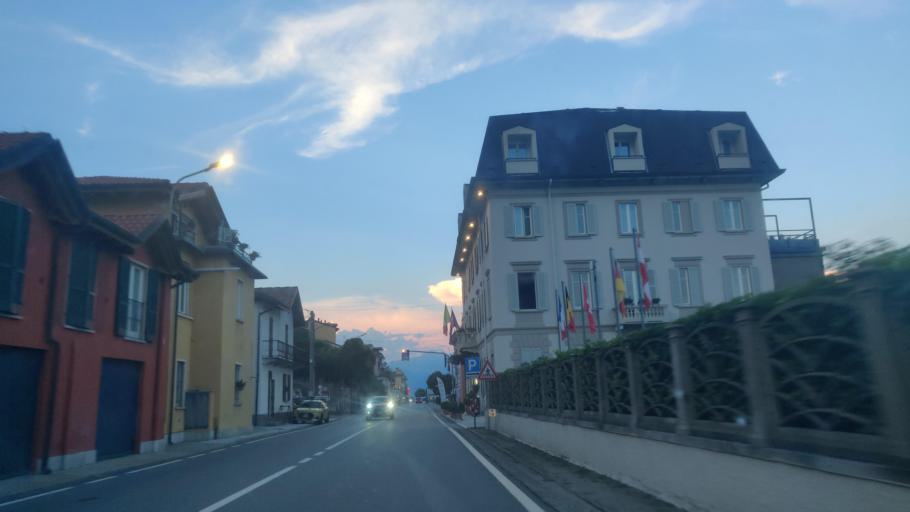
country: IT
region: Piedmont
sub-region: Provincia Verbano-Cusio-Ossola
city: Ghiffa
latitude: 45.9558
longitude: 8.6161
